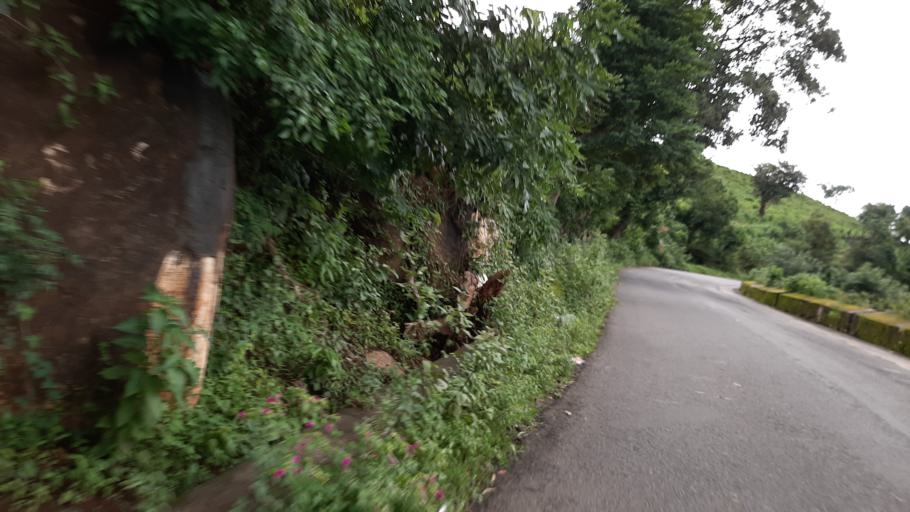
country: IN
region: Andhra Pradesh
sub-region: Vizianagaram District
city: Salur
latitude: 18.2404
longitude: 83.0268
